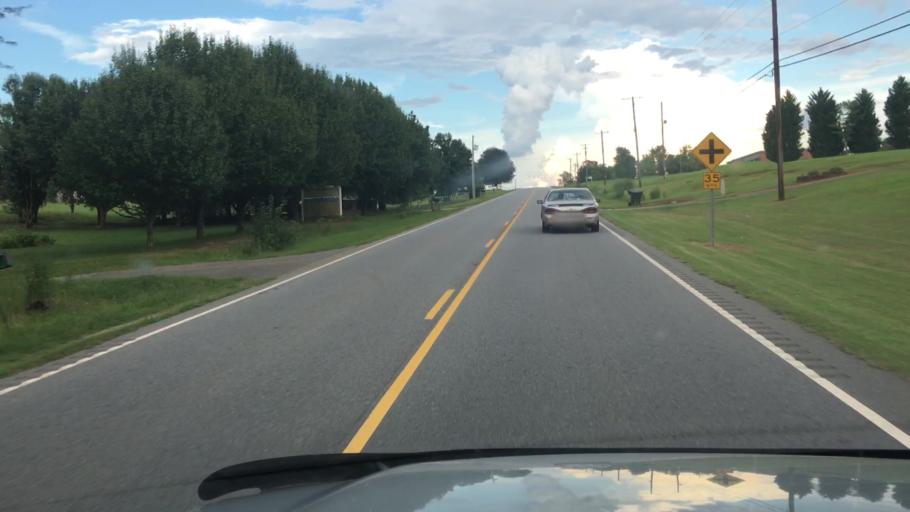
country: US
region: South Carolina
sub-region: Spartanburg County
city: Mayo
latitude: 35.1263
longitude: -81.7790
